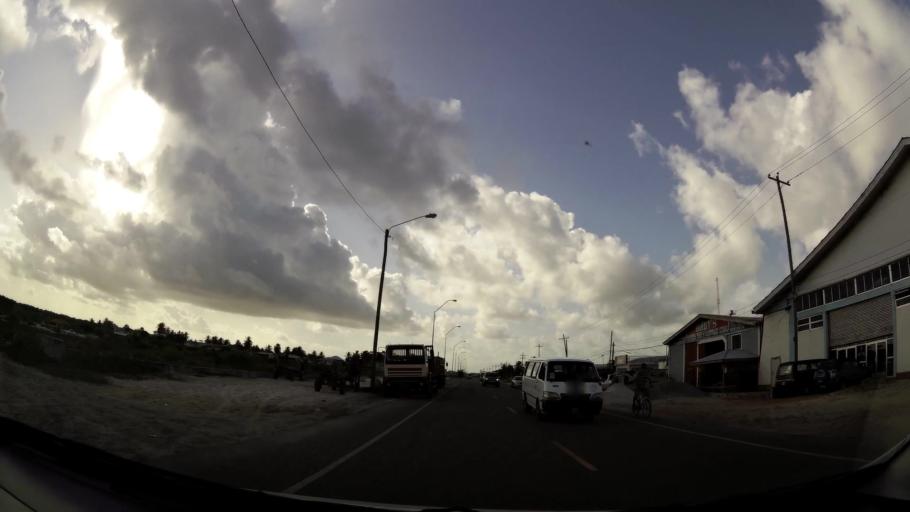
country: GY
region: Demerara-Mahaica
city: Georgetown
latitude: 6.8015
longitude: -58.0439
